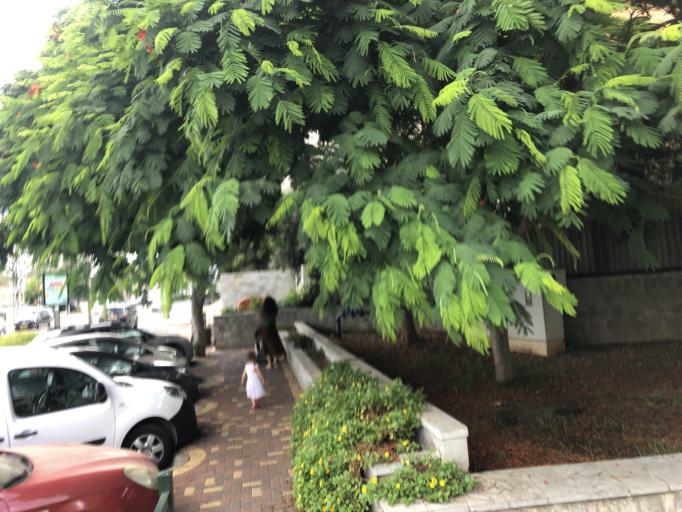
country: IL
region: Central District
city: Yehud
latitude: 32.0303
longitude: 34.8861
